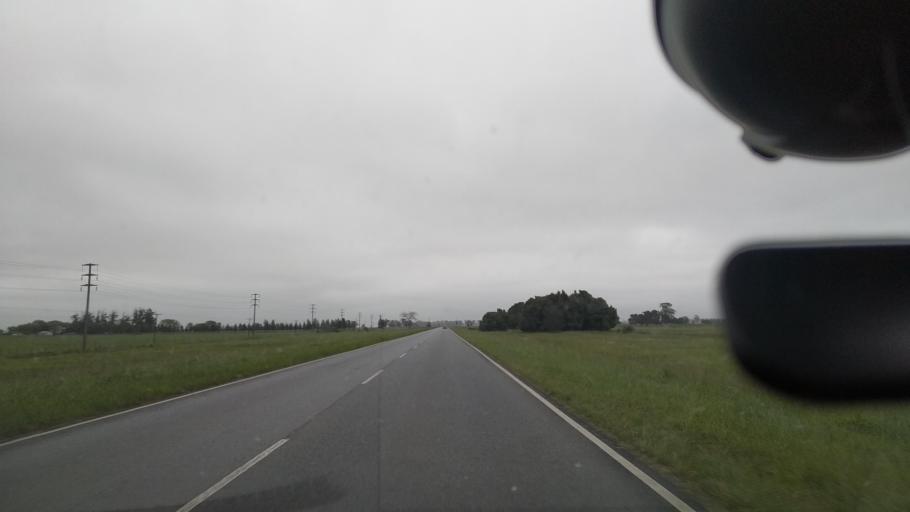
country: AR
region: Buenos Aires
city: Veronica
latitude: -35.3502
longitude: -57.4305
